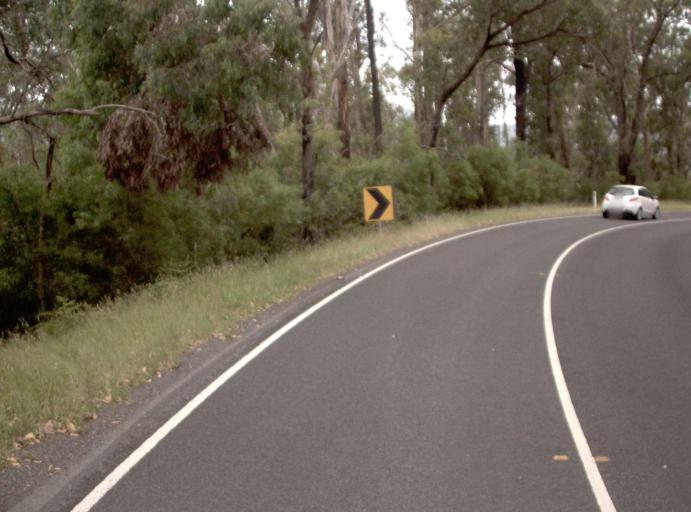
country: AU
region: Victoria
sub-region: Yarra Ranges
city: Healesville
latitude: -37.6422
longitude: 145.5766
